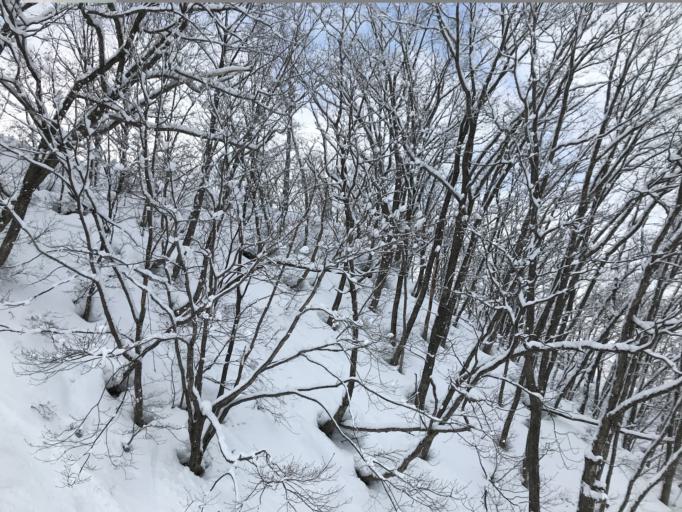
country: JP
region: Nagano
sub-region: Kitaazumi Gun
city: Hakuba
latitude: 36.7102
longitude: 137.8231
